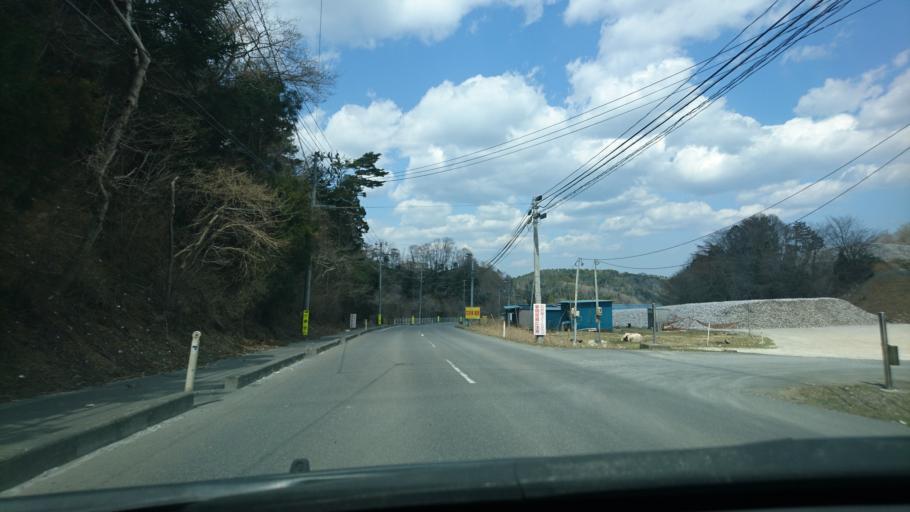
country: JP
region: Miyagi
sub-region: Oshika Gun
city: Onagawa Cho
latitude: 38.4486
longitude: 141.4896
